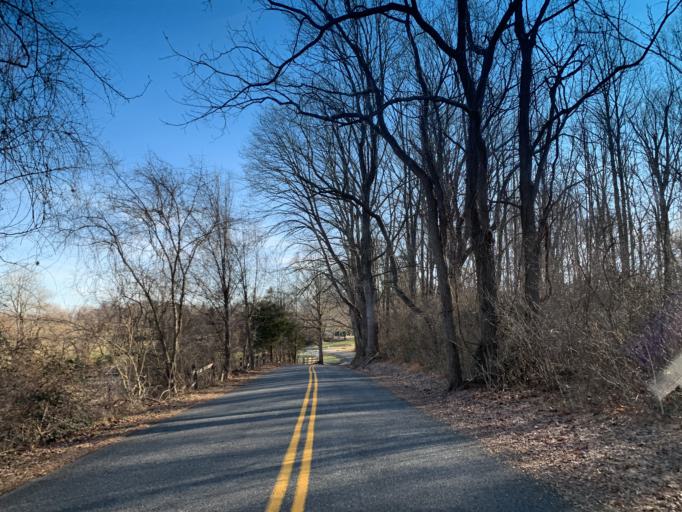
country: US
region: Maryland
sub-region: Harford County
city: South Bel Air
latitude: 39.5818
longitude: -76.2509
